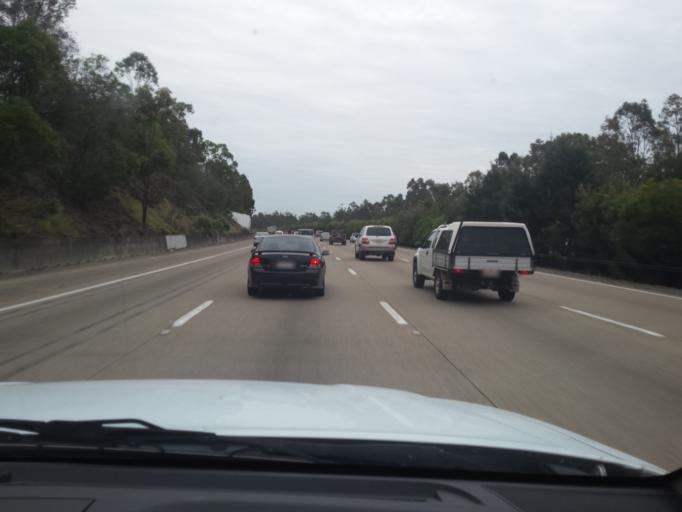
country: AU
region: Queensland
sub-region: Gold Coast
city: Ormeau Hills
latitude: -27.8297
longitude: 153.3003
